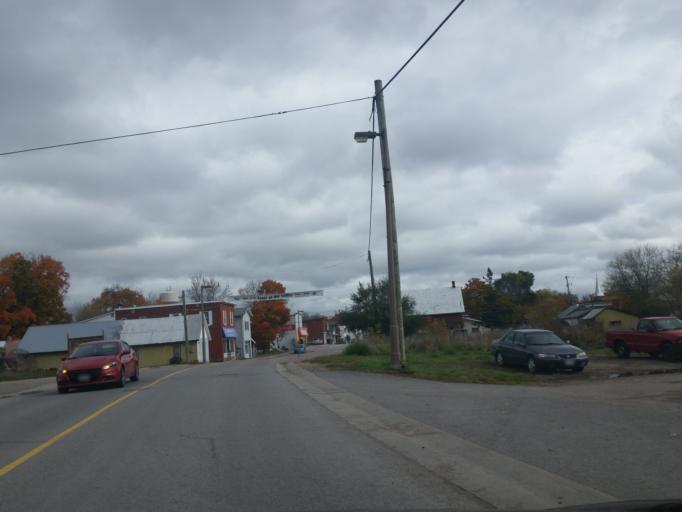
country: CA
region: Ontario
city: Renfrew
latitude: 45.6262
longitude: -76.8870
